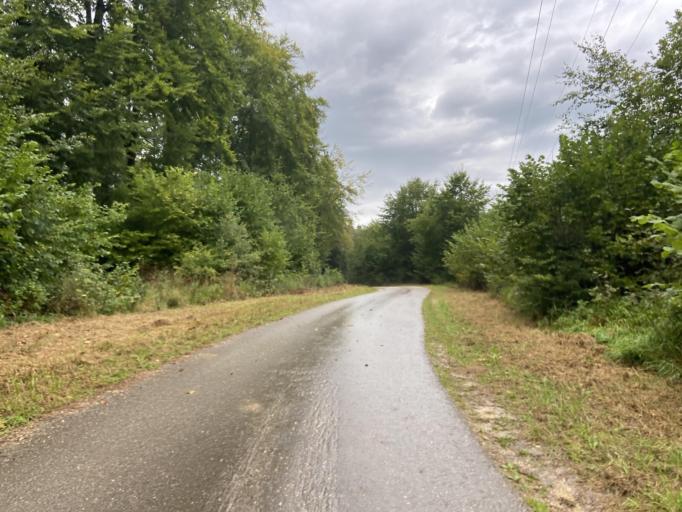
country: DE
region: Baden-Wuerttemberg
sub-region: Tuebingen Region
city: Bingen
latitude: 48.1301
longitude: 9.2625
